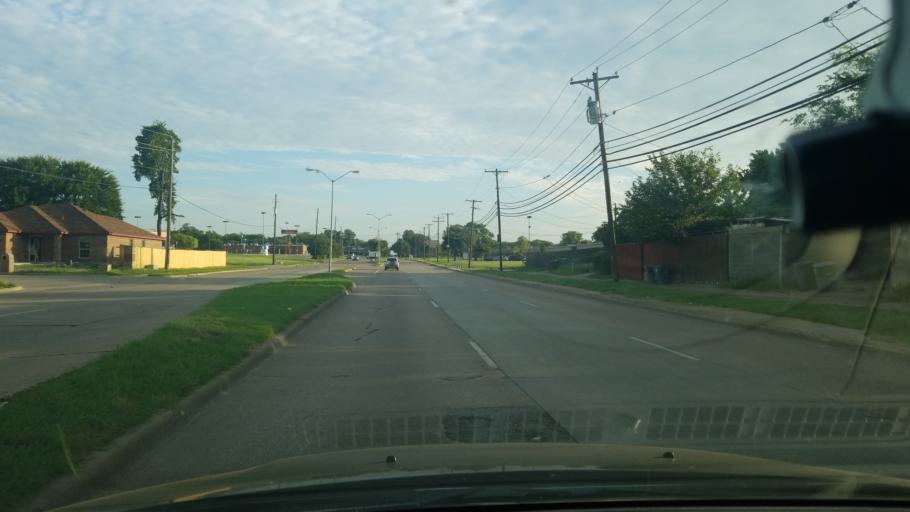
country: US
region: Texas
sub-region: Dallas County
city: Balch Springs
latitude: 32.7450
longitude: -96.6483
